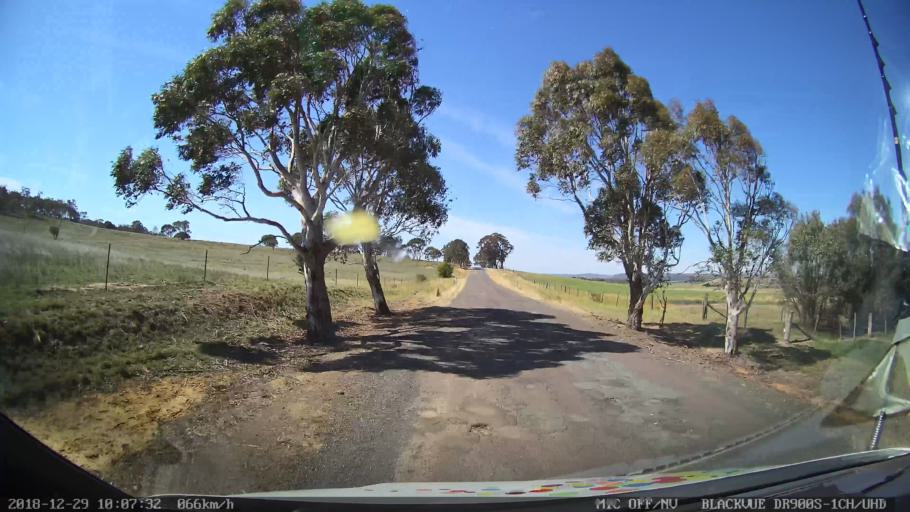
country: AU
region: New South Wales
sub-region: Yass Valley
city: Gundaroo
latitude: -34.8537
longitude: 149.4528
